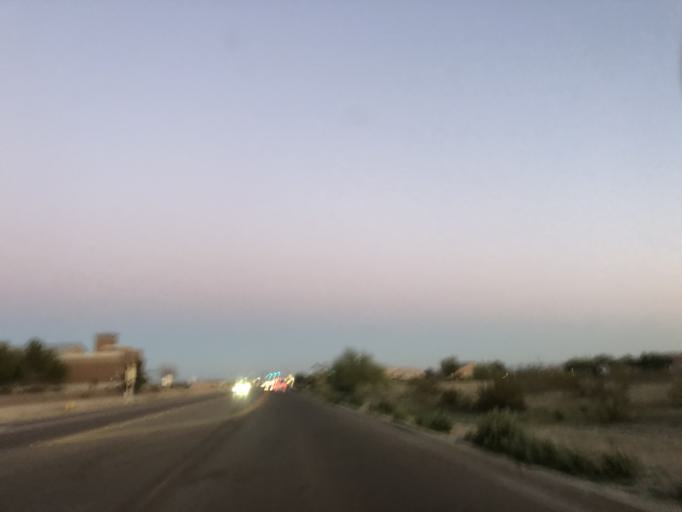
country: US
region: Arizona
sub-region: Maricopa County
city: Citrus Park
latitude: 33.4936
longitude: -112.4934
